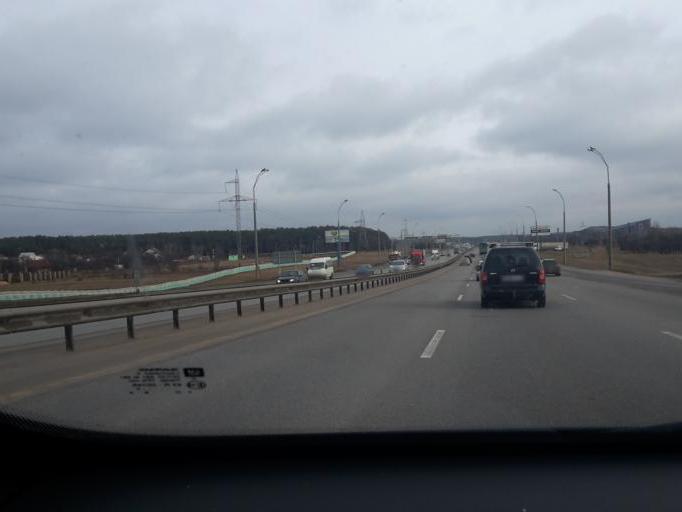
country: BY
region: Minsk
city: Zhdanovichy
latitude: 53.9455
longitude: 27.4386
